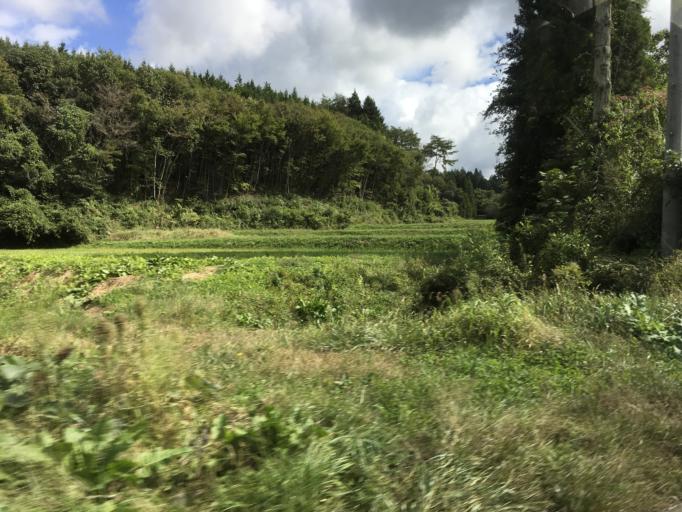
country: JP
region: Iwate
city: Ichinoseki
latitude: 38.8342
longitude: 141.3560
